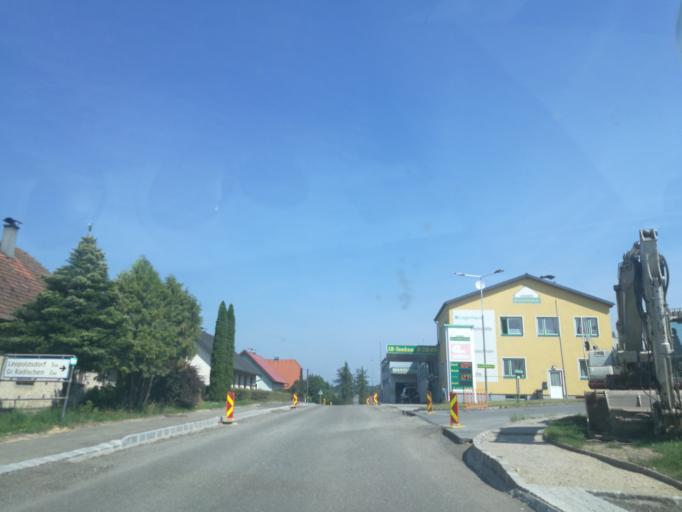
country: AT
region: Lower Austria
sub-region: Politischer Bezirk Gmund
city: Eisgarn
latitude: 48.9161
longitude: 15.1055
